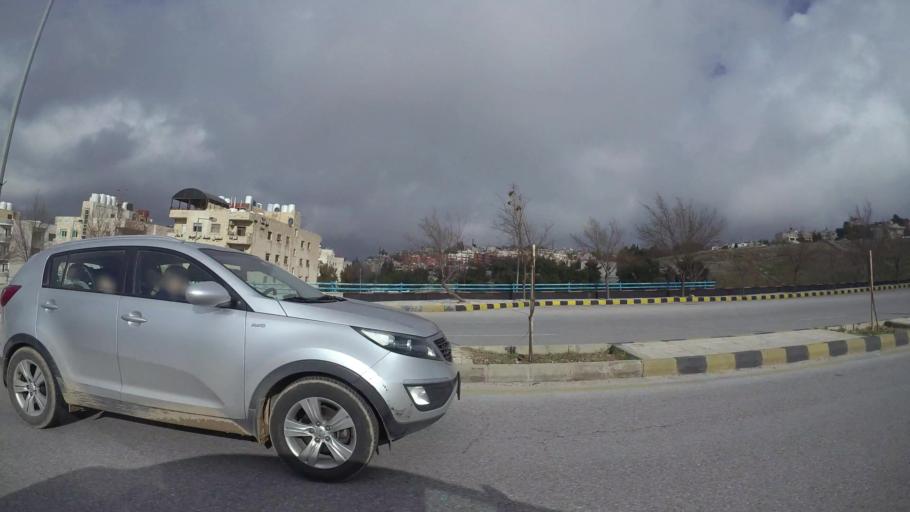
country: JO
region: Amman
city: Al Jubayhah
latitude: 32.0543
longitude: 35.8704
